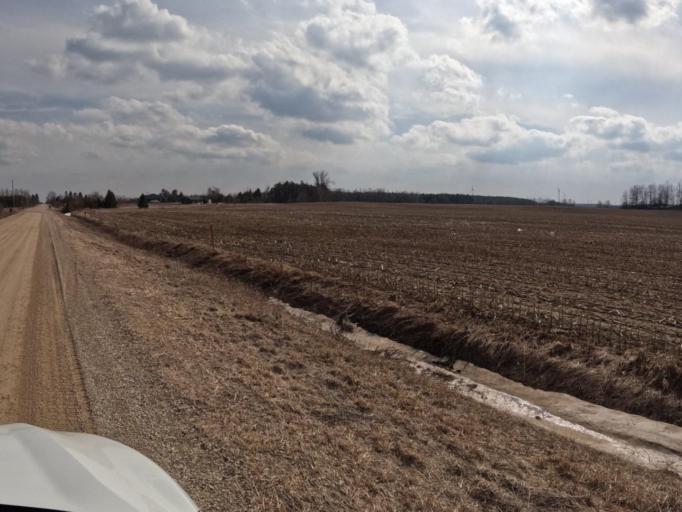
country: CA
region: Ontario
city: Shelburne
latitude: 43.9476
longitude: -80.3124
